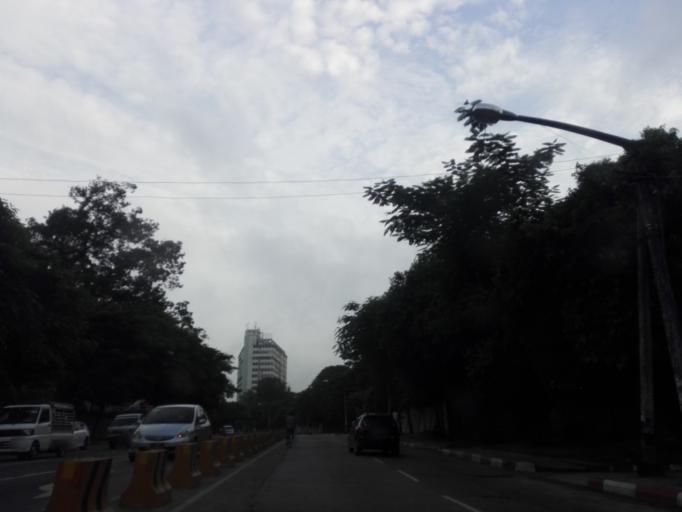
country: MM
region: Yangon
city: Yangon
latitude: 16.8048
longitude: 96.1424
